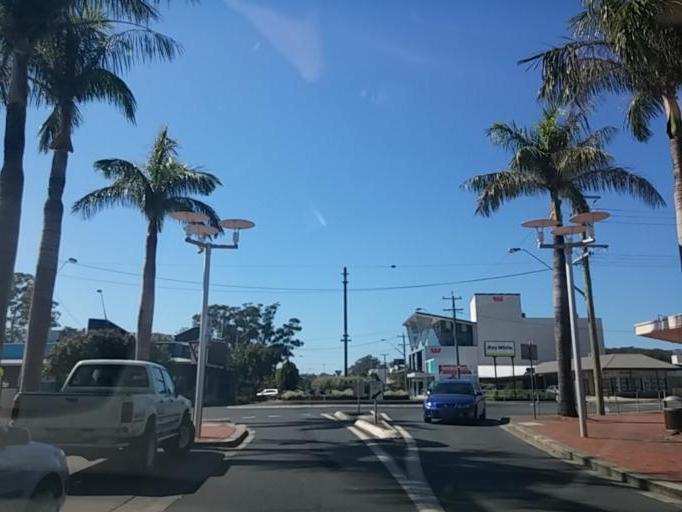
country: AU
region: New South Wales
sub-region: Coffs Harbour
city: Coffs Harbour
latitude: -30.2977
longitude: 153.1160
